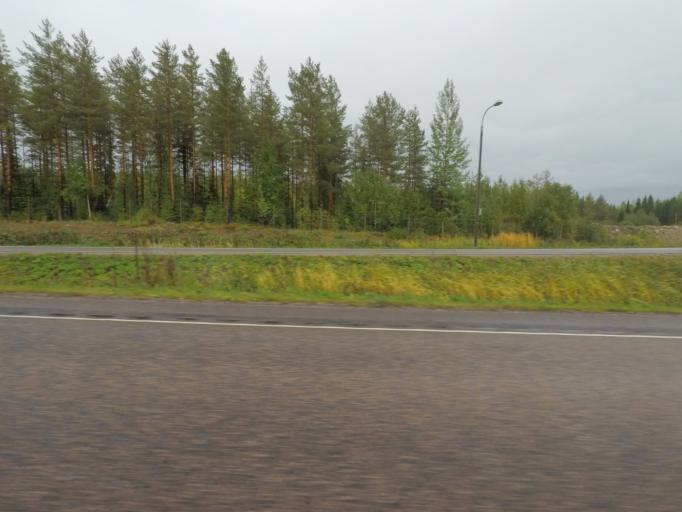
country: FI
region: Northern Savo
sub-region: Varkaus
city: Varkaus
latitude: 62.2619
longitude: 27.8697
